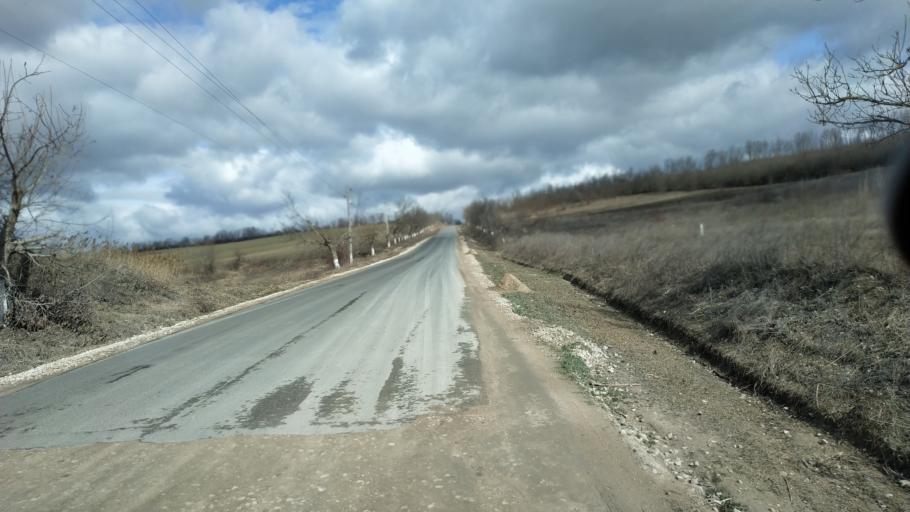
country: MD
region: Stinga Nistrului
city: Bucovat
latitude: 47.1977
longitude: 28.4899
